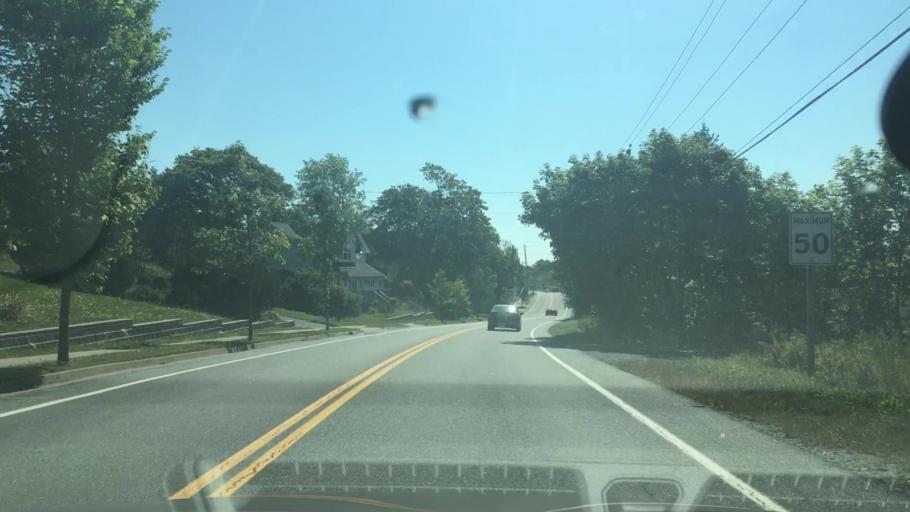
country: CA
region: Nova Scotia
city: New Glasgow
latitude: 44.9271
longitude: -62.5428
